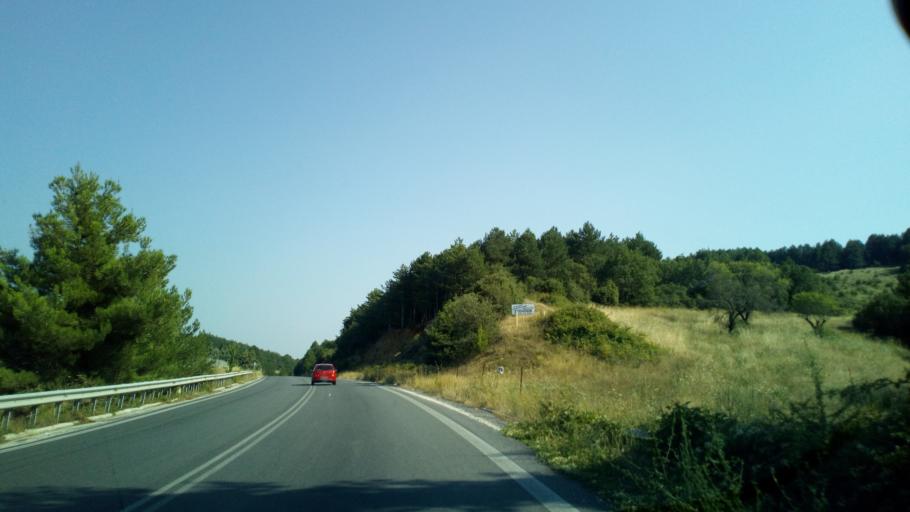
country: GR
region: Central Macedonia
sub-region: Nomos Chalkidikis
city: Polygyros
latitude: 40.4025
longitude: 23.4223
